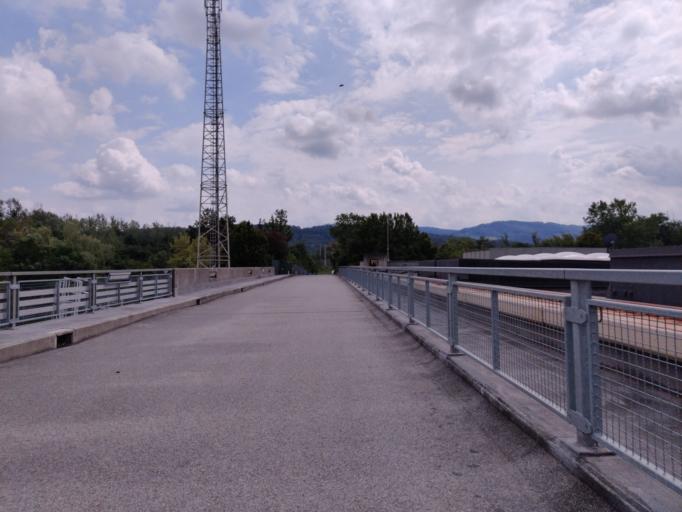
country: AT
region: Lower Austria
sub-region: Politischer Bezirk Melk
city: Melk
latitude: 48.2227
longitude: 15.3045
